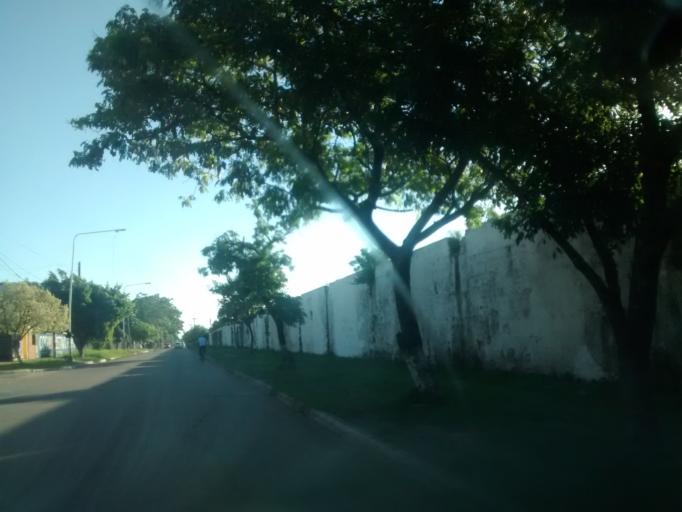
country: AR
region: Chaco
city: Resistencia
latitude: -27.4549
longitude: -59.0103
